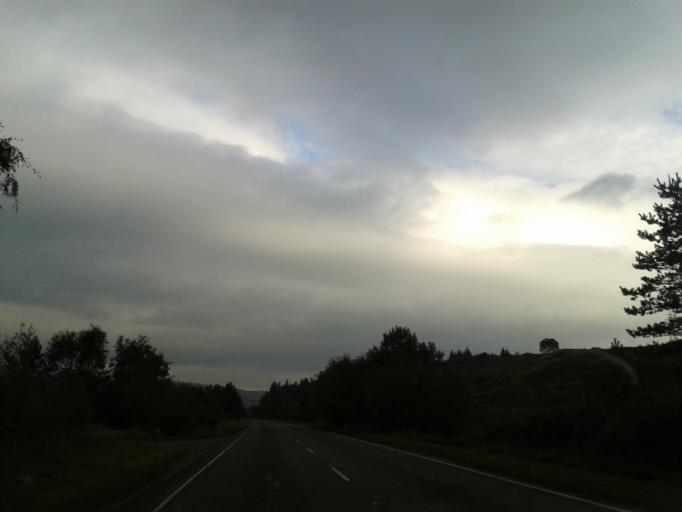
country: GB
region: Scotland
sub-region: Highland
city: Spean Bridge
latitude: 57.1625
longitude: -4.8864
